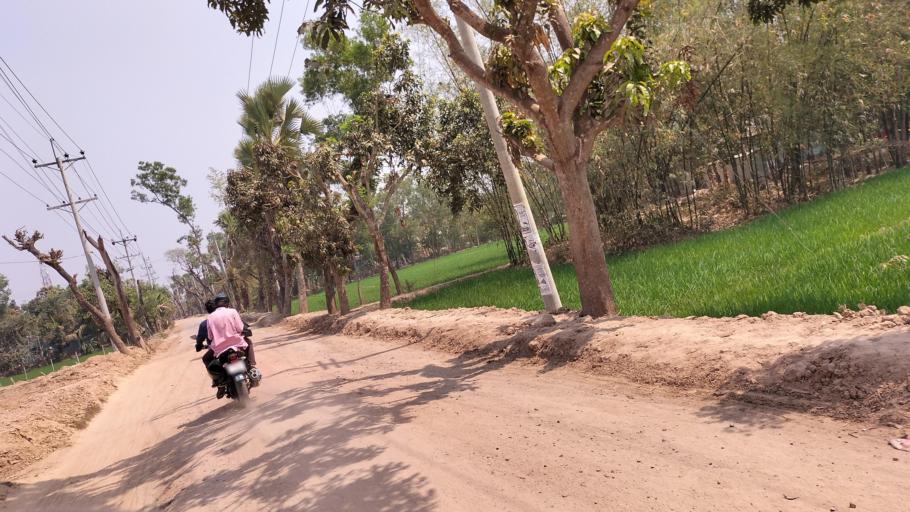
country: BD
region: Dhaka
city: Sakhipur
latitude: 24.3070
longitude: 90.3127
